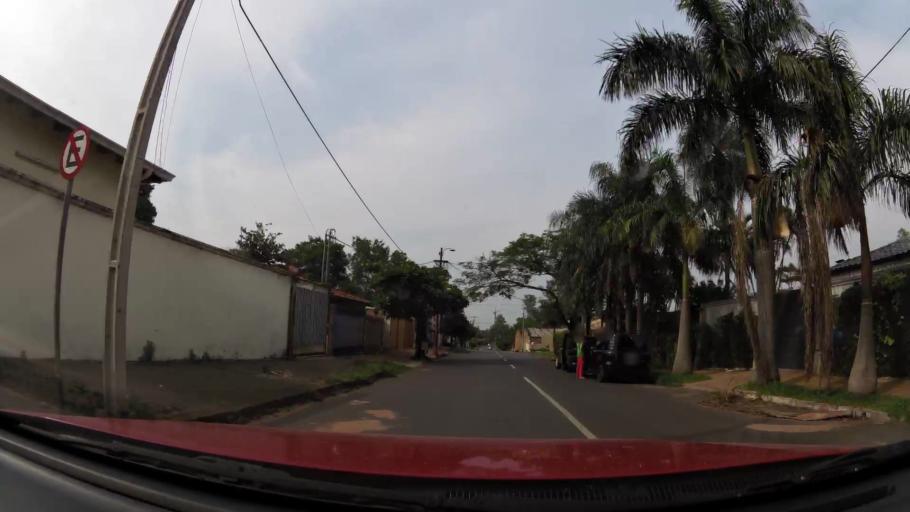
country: PY
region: Central
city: Fernando de la Mora
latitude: -25.2963
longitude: -57.5541
